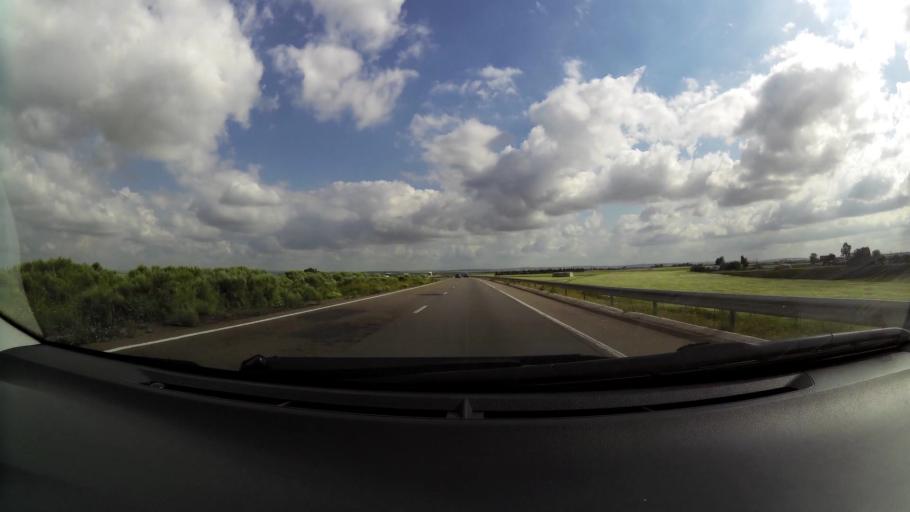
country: MA
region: Chaouia-Ouardigha
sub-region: Settat Province
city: Berrechid
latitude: 33.1947
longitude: -7.5760
